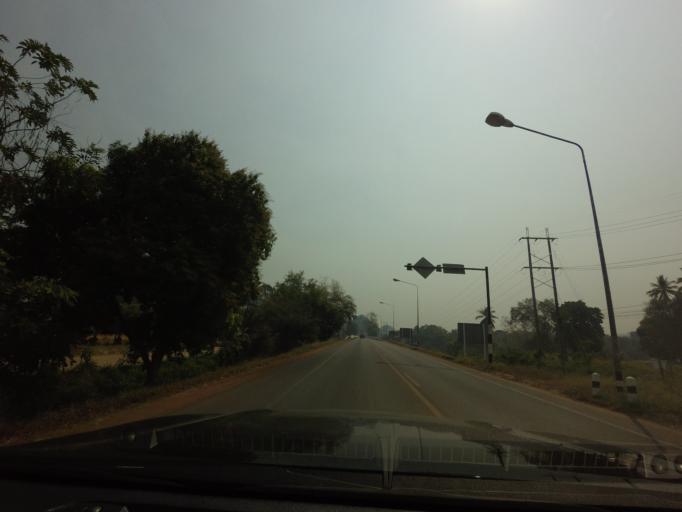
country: TH
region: Kanchanaburi
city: Thong Pha Phum
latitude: 14.7382
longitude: 98.6338
